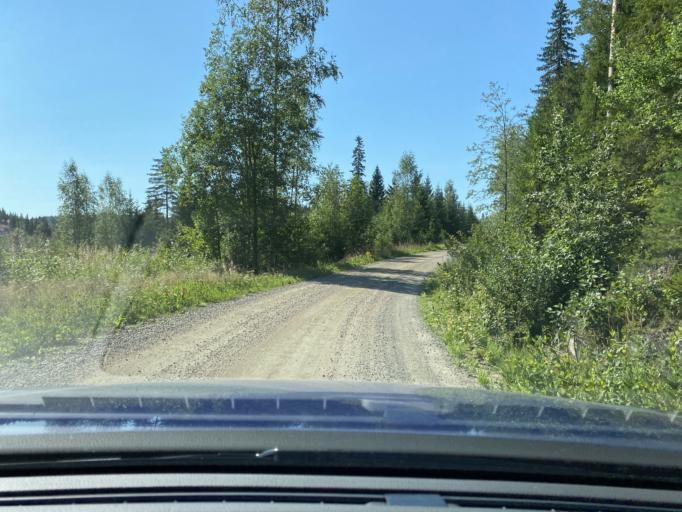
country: FI
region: Central Finland
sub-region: Jaemsae
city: Jaemsae
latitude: 61.8562
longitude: 25.3935
